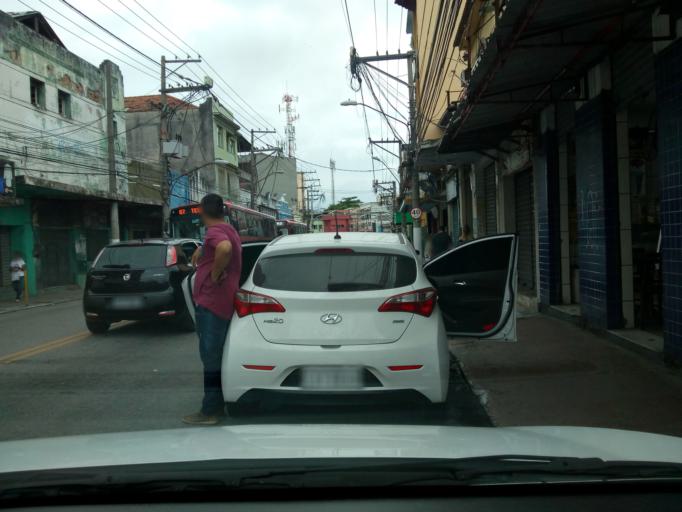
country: BR
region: Rio de Janeiro
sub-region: Niteroi
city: Niteroi
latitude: -22.8611
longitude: -43.1025
